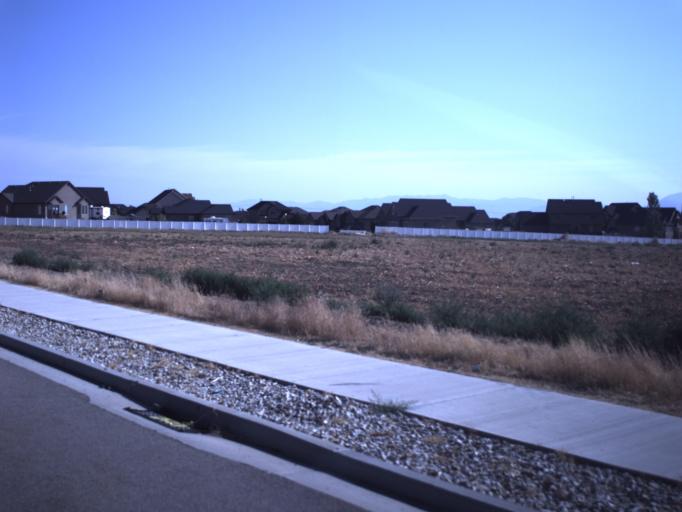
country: US
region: Utah
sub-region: Salt Lake County
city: Herriman
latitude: 40.5136
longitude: -112.0042
